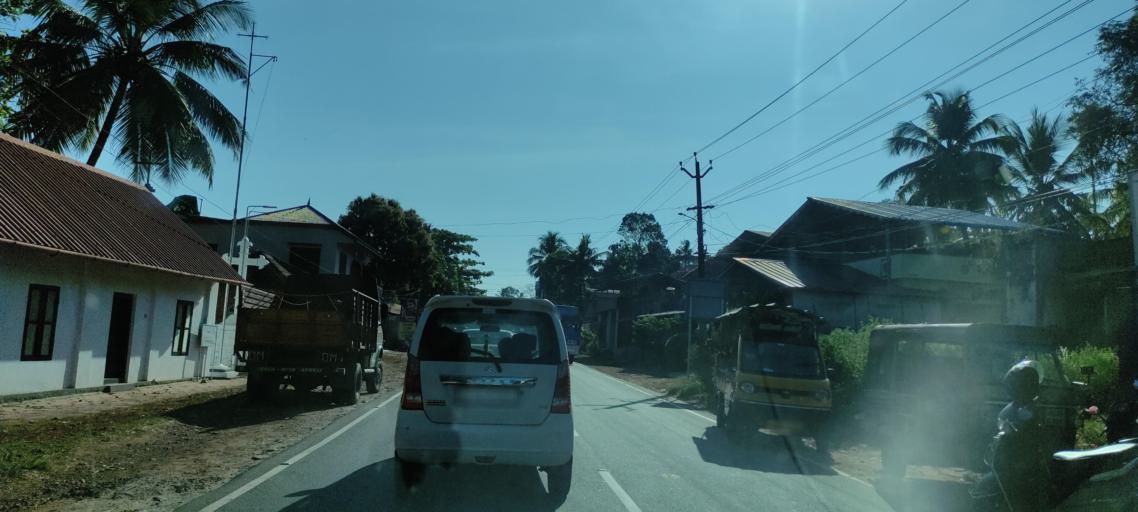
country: IN
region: Kerala
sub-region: Pattanamtitta
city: Adur
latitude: 9.1733
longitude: 76.6458
